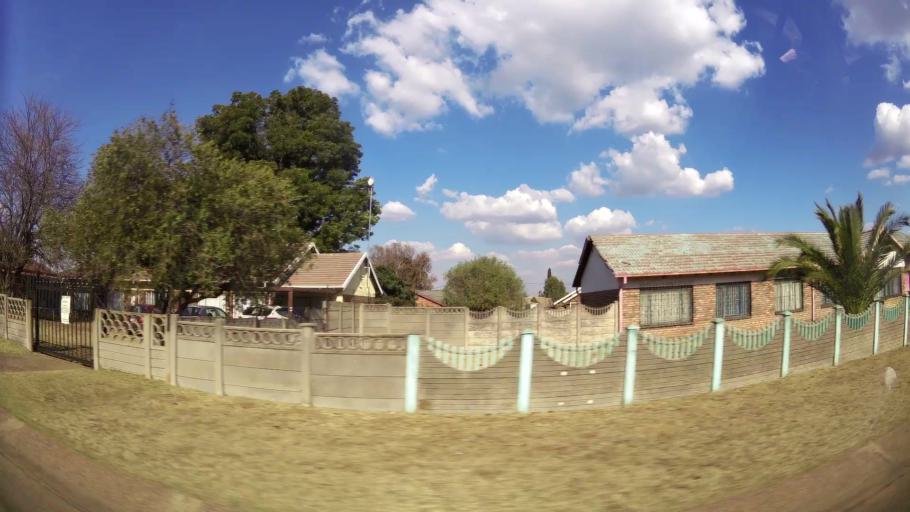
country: ZA
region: Mpumalanga
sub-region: Nkangala District Municipality
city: Witbank
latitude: -25.9169
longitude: 29.2264
